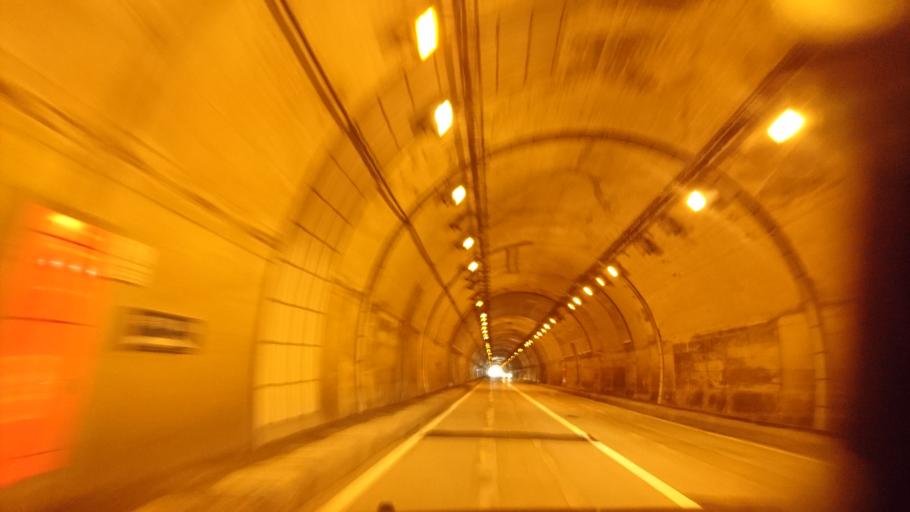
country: JP
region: Iwate
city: Shizukuishi
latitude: 39.6922
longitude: 140.7860
